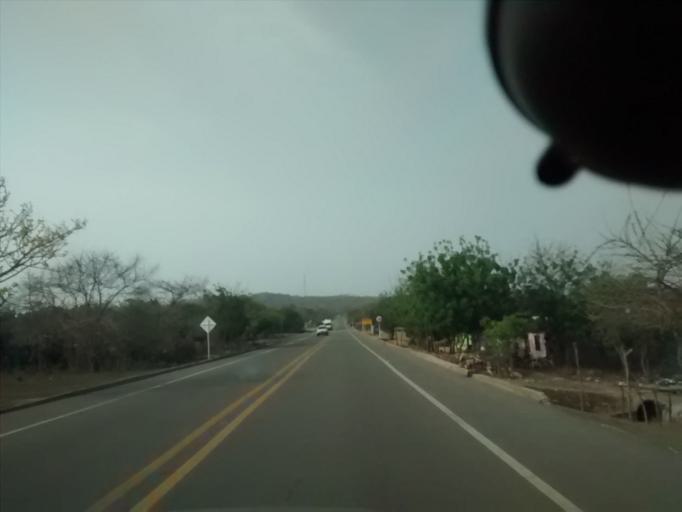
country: CO
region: Bolivar
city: Santa Catalina
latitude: 10.7320
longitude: -75.2644
